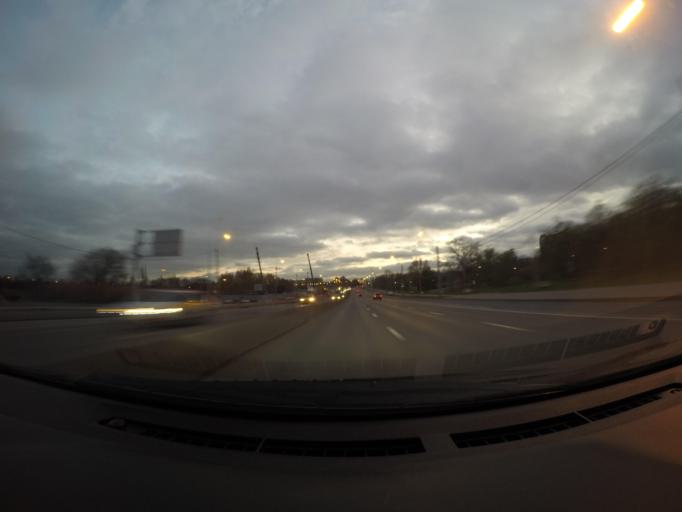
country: RU
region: Moscow
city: Kolomenskoye
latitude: 55.6629
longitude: 37.6568
